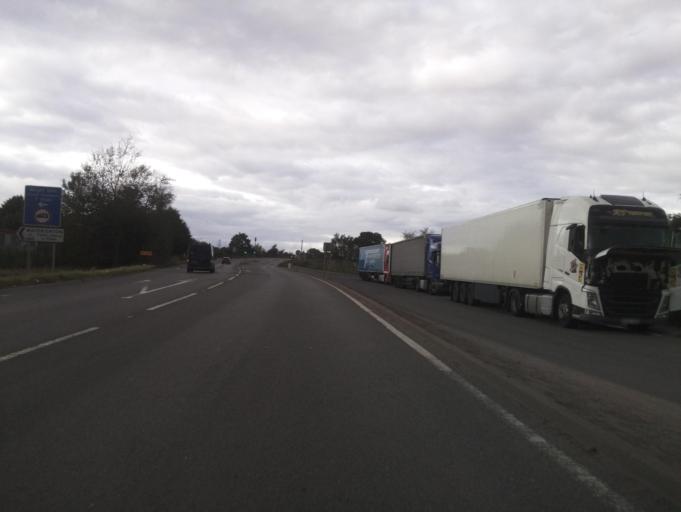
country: GB
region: England
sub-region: Warwickshire
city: Water Orton
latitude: 52.5167
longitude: -1.7208
